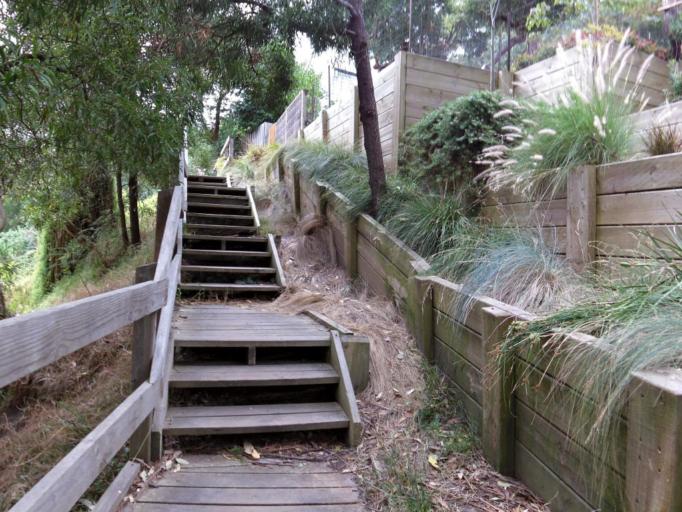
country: AU
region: Victoria
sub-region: Frankston
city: Frankston
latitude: -38.1574
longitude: 145.1103
